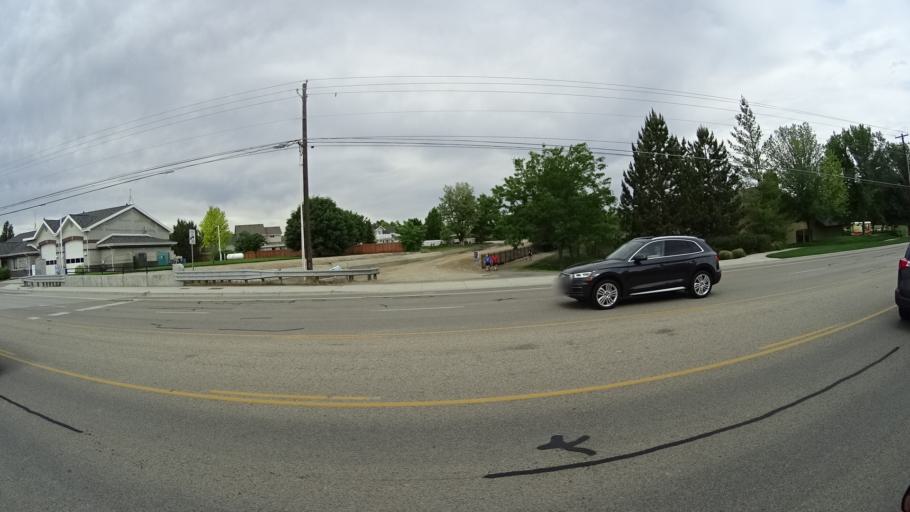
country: US
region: Idaho
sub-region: Ada County
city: Meridian
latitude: 43.5829
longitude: -116.3544
